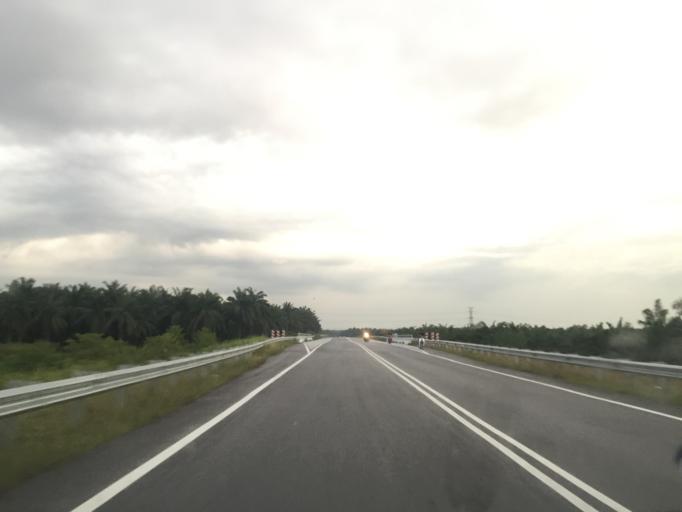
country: MY
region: Penang
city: Tasek Glugor
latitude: 5.5280
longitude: 100.5313
